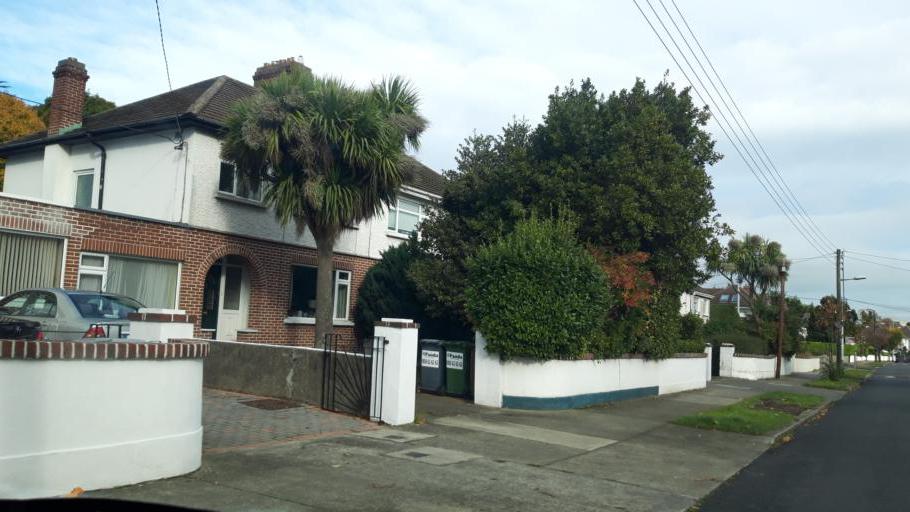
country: IE
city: Milltown
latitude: 53.2979
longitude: -6.2391
